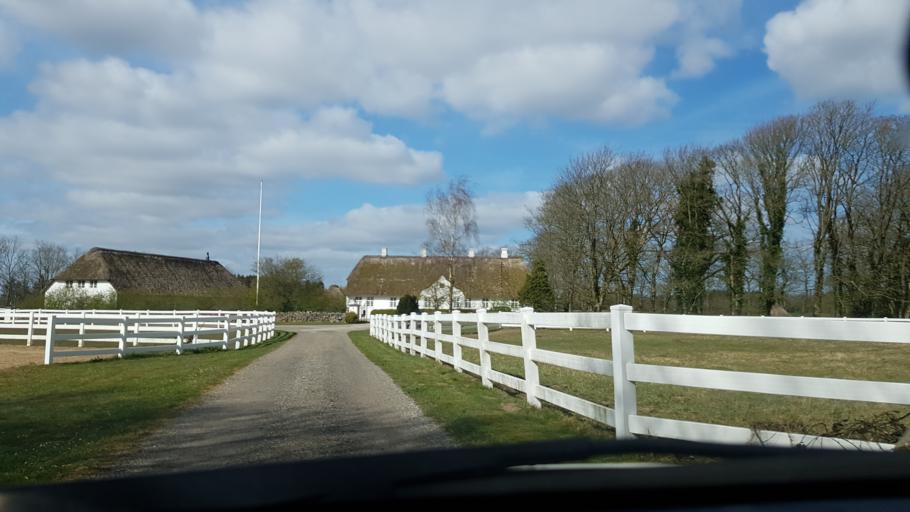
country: DK
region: South Denmark
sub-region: Haderslev Kommune
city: Gram
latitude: 55.2980
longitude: 8.9844
